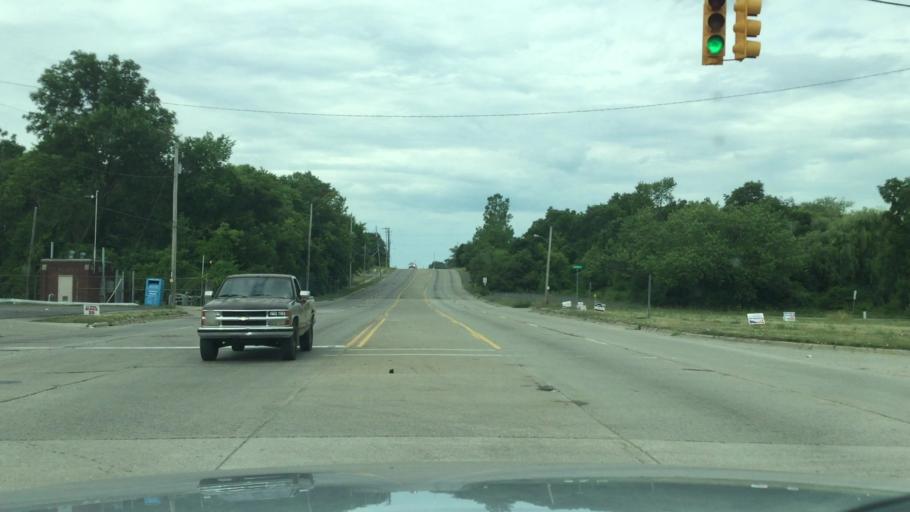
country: US
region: Michigan
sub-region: Genesee County
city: Beecher
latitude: 43.0758
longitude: -83.6846
